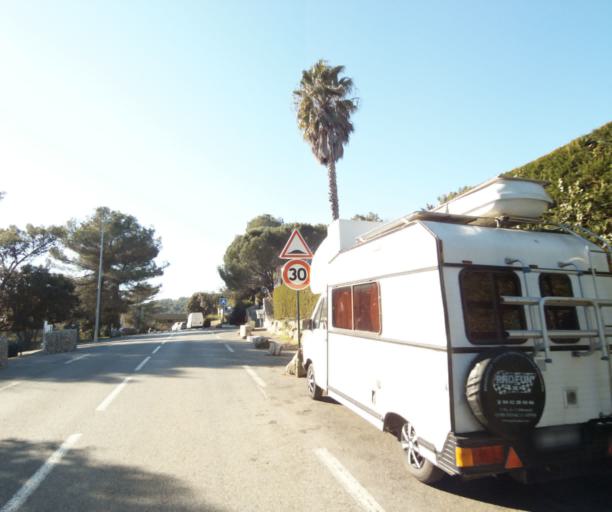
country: FR
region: Provence-Alpes-Cote d'Azur
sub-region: Departement des Alpes-Maritimes
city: Biot
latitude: 43.6078
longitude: 7.0704
